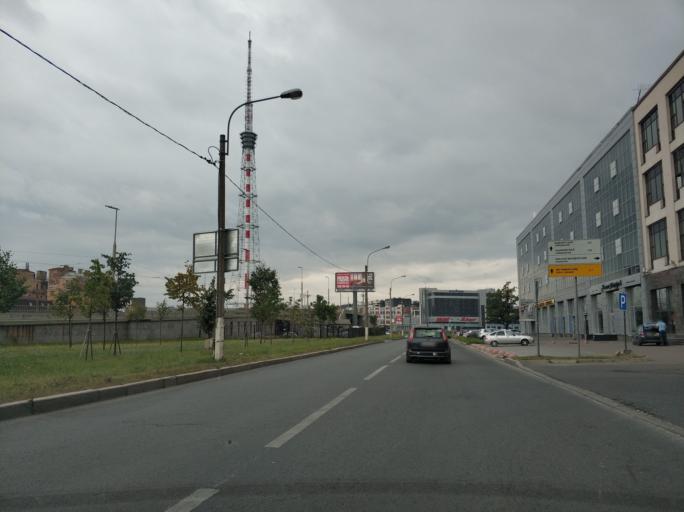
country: RU
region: Leningrad
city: Sampsonievskiy
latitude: 59.9809
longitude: 30.3243
